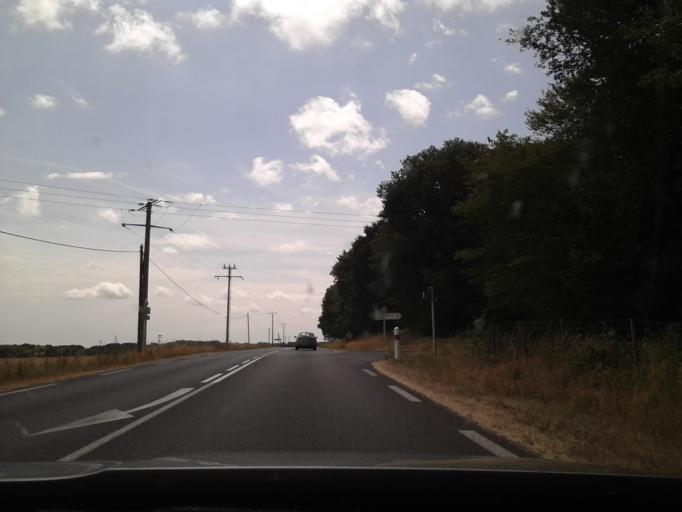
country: FR
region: Centre
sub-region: Departement d'Indre-et-Loire
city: Poce-sur-Cisse
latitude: 47.5202
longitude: 0.9954
